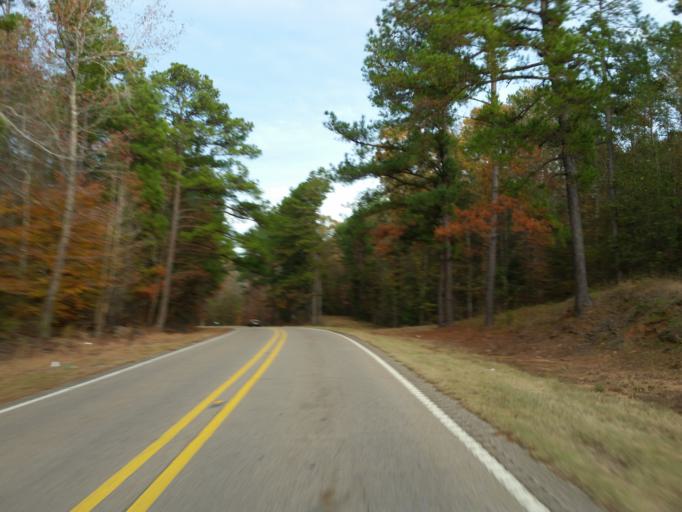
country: US
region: Mississippi
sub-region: Lauderdale County
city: Marion
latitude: 32.4127
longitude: -88.5440
